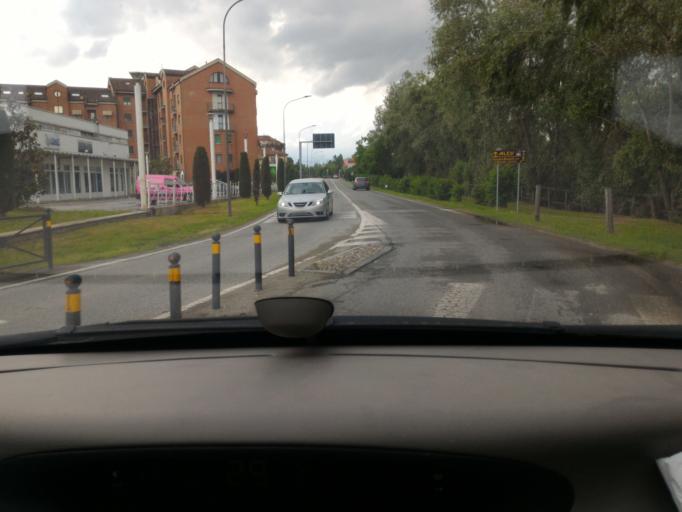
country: IT
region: Piedmont
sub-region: Provincia di Cuneo
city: Savigliano
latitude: 44.6506
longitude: 7.6524
